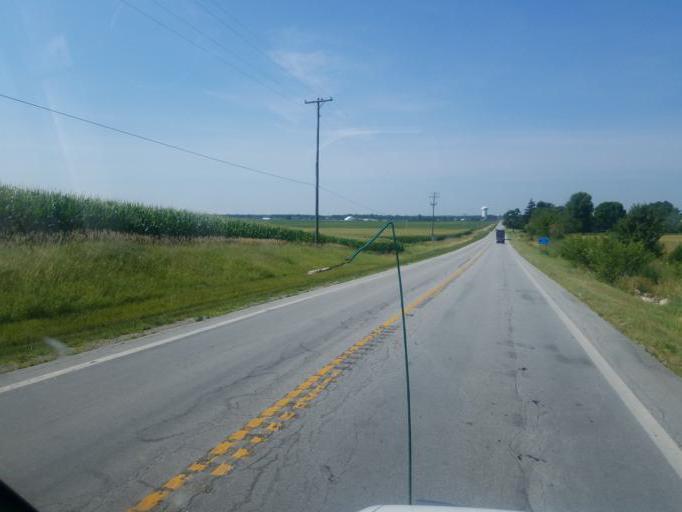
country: US
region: Ohio
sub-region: Union County
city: Marysville
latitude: 40.2823
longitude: -83.3506
